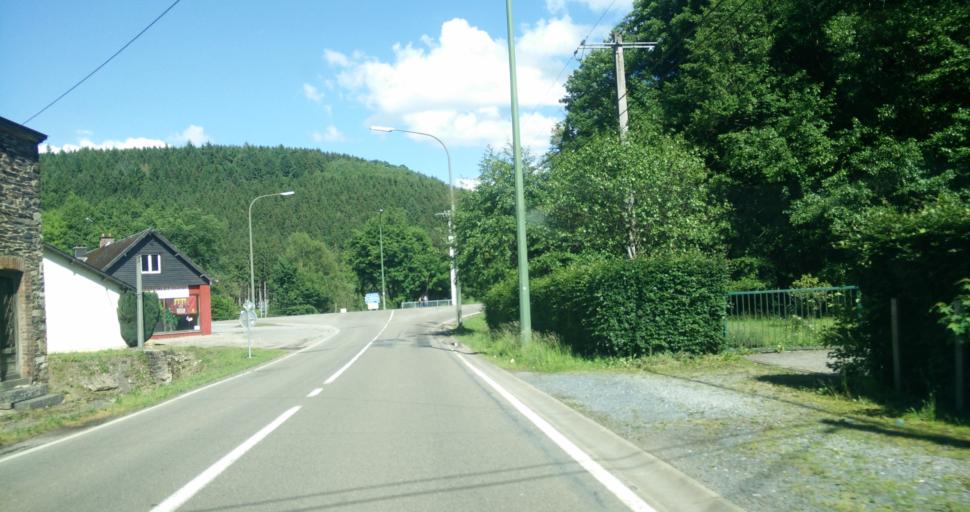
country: BE
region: Wallonia
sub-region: Province du Luxembourg
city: La Roche-en-Ardenne
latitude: 50.1898
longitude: 5.5385
